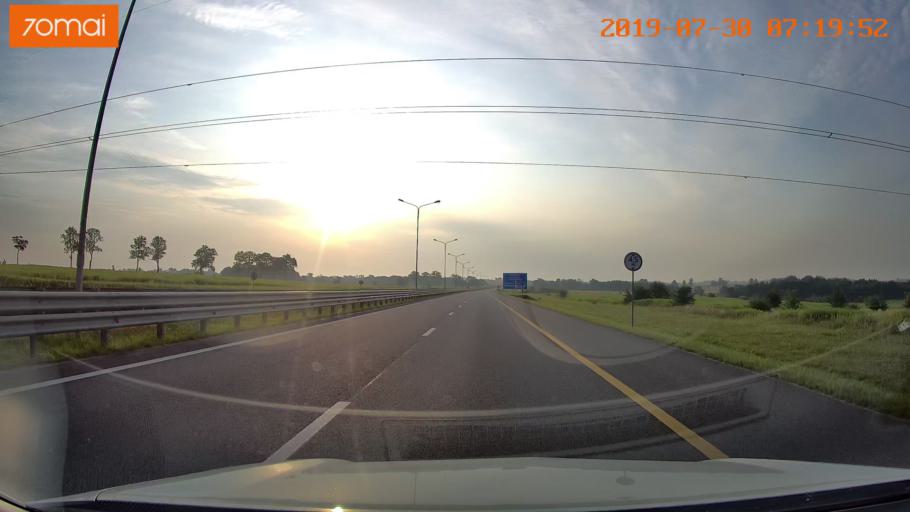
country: RU
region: Kaliningrad
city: Bol'shoe Isakovo
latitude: 54.7011
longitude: 20.6909
